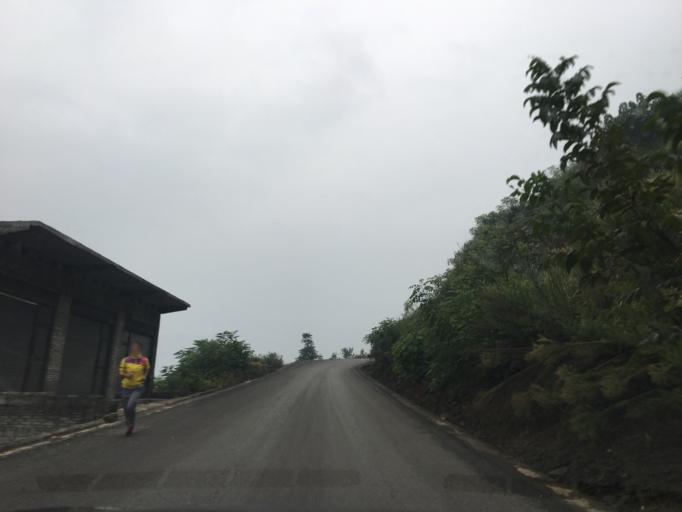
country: CN
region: Guizhou Sheng
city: Liupanshui
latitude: 26.0634
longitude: 105.1379
